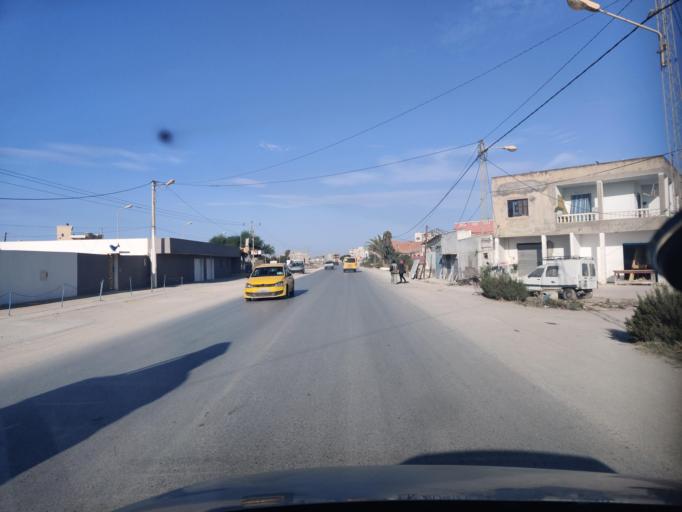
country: TN
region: Ariana
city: Ariana
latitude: 36.9565
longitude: 10.2105
